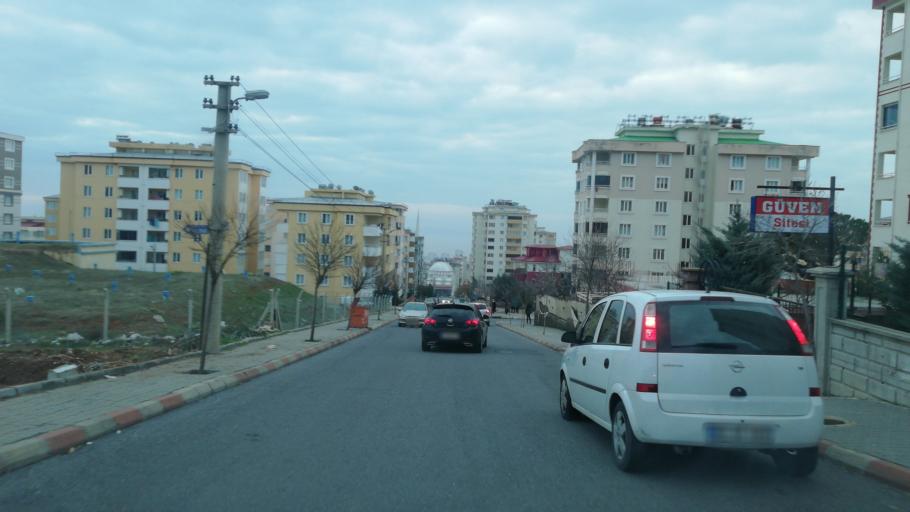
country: TR
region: Kahramanmaras
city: Kahramanmaras
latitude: 37.5981
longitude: 36.8950
